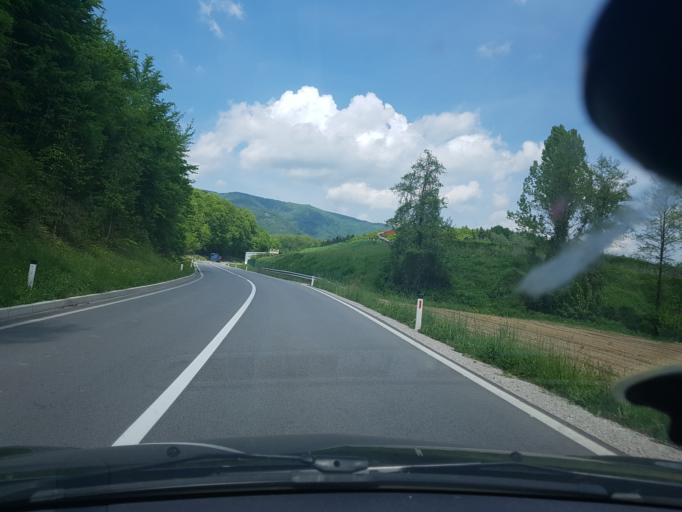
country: SI
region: Rogatec
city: Rogatec
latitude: 46.2341
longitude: 15.6728
